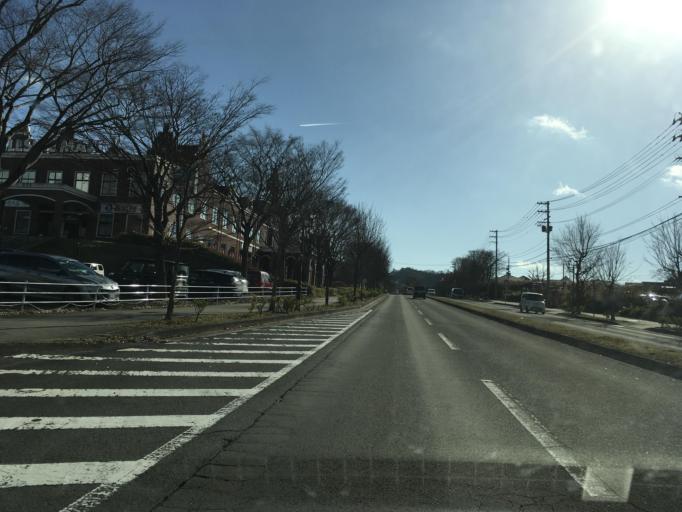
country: JP
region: Miyagi
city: Sendai
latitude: 38.2582
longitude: 140.7633
